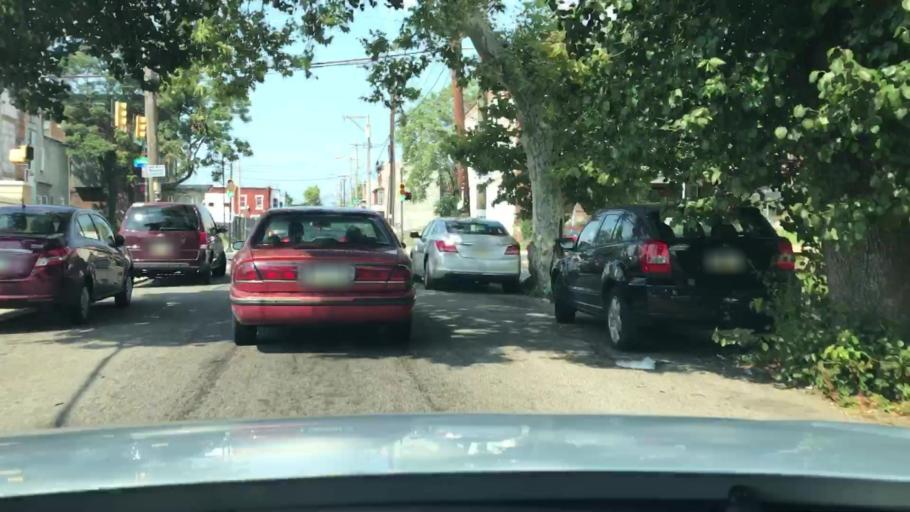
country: US
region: Pennsylvania
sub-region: Philadelphia County
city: Philadelphia
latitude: 39.9933
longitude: -75.1525
